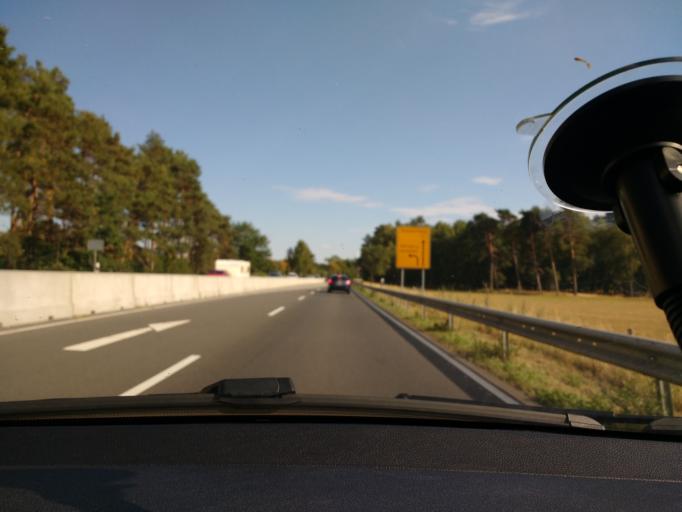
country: DE
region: Lower Saxony
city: Ribbesbuttel
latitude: 52.4483
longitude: 10.5361
